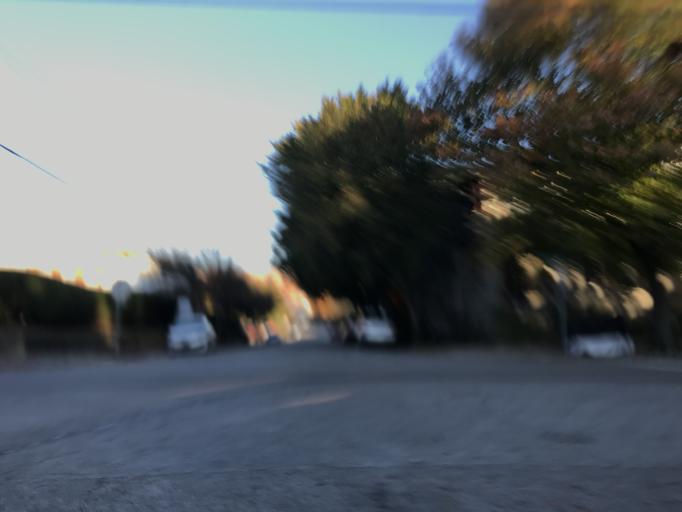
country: US
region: Kentucky
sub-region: Jefferson County
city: Louisville
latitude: 38.2410
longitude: -85.7295
